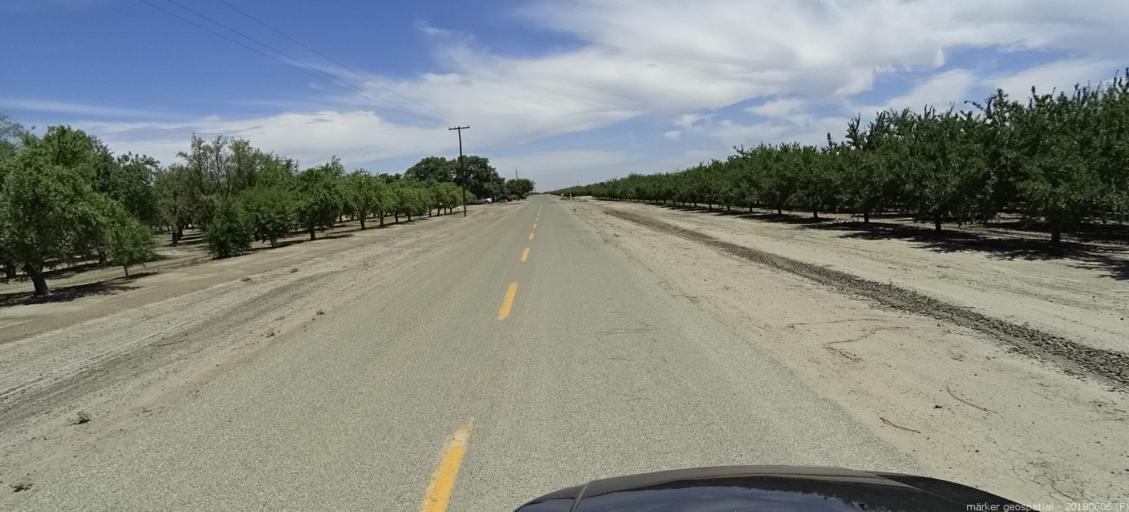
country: US
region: California
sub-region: Fresno County
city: Firebaugh
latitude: 36.8495
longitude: -120.3909
